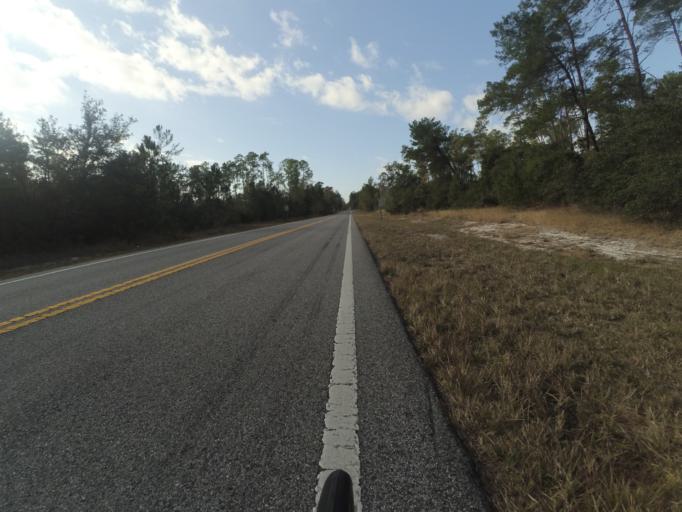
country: US
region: Florida
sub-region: Lake County
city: Astor
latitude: 29.1191
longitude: -81.6162
